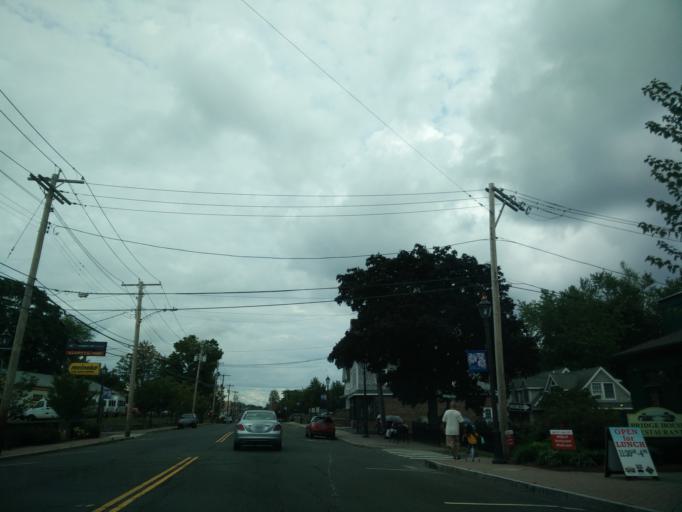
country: US
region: Connecticut
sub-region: Fairfield County
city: Stratford
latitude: 41.2002
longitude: -73.1069
